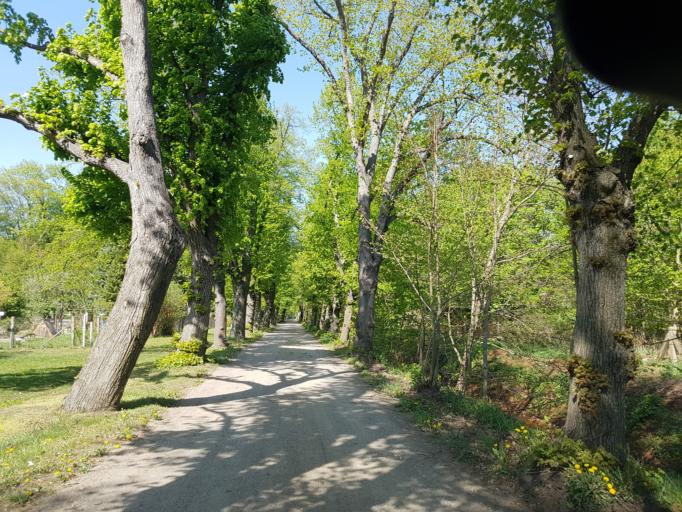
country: DE
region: Brandenburg
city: Finsterwalde
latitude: 51.6273
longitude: 13.6942
